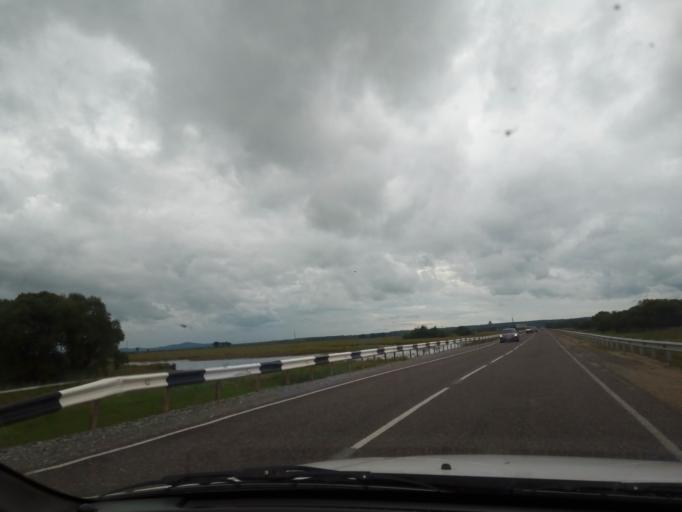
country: RU
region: Primorskiy
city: Dal'nerechensk
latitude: 45.9152
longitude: 133.7706
